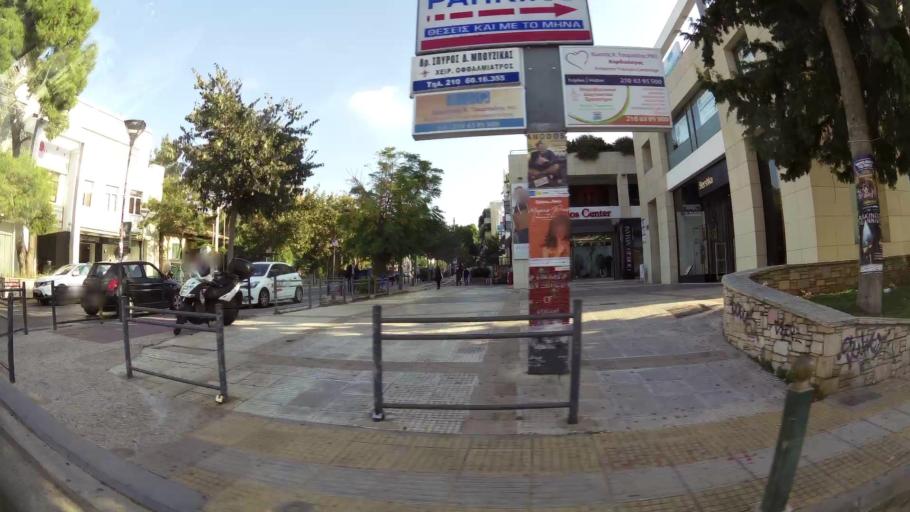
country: GR
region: Attica
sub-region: Nomarchia Athinas
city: Agia Paraskevi
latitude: 38.0117
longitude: 23.8225
